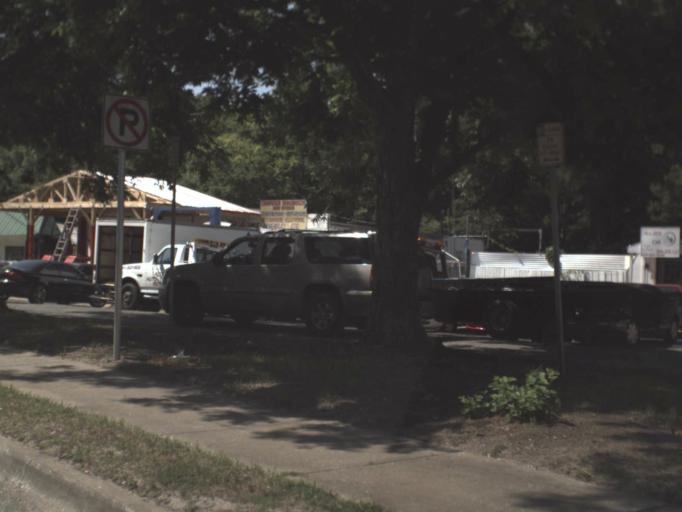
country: US
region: Florida
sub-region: Duval County
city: Jacksonville
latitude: 30.4153
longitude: -81.6952
